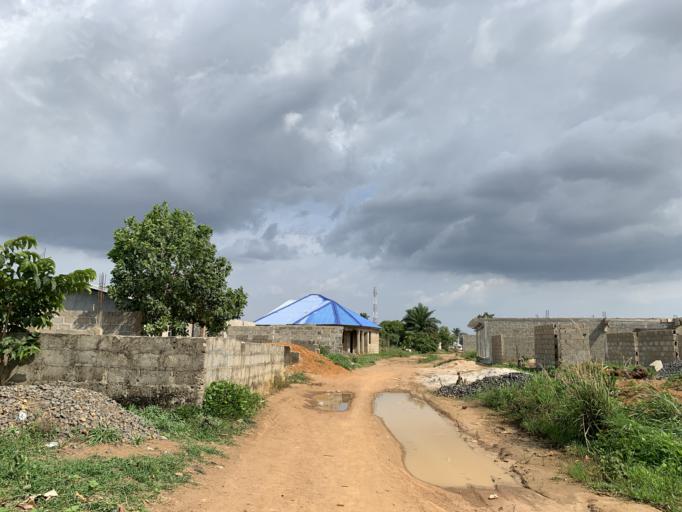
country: SL
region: Western Area
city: Waterloo
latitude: 8.3532
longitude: -13.0432
